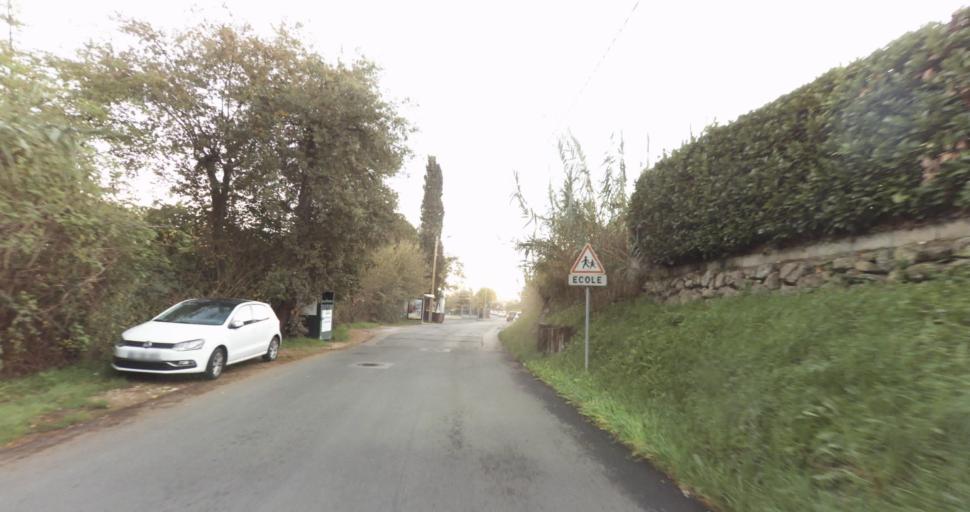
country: FR
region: Provence-Alpes-Cote d'Azur
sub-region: Departement des Alpes-Maritimes
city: Vence
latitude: 43.7210
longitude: 7.1276
